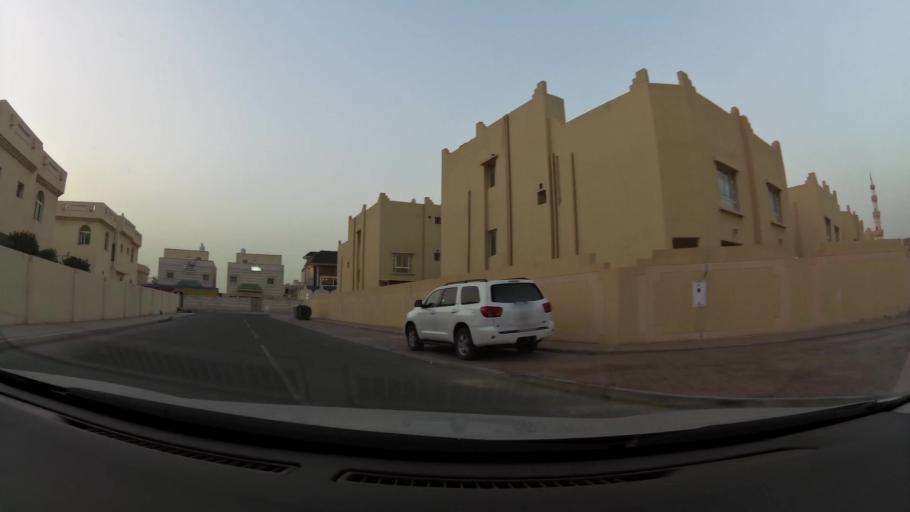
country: QA
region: Baladiyat ar Rayyan
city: Ar Rayyan
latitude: 25.2515
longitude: 51.4622
